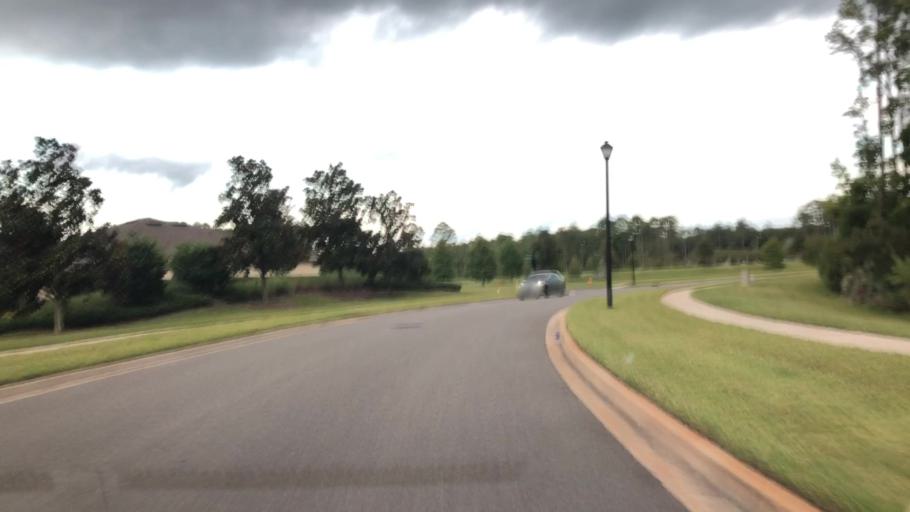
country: US
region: Florida
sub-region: Saint Johns County
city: Palm Valley
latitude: 30.1158
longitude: -81.4521
